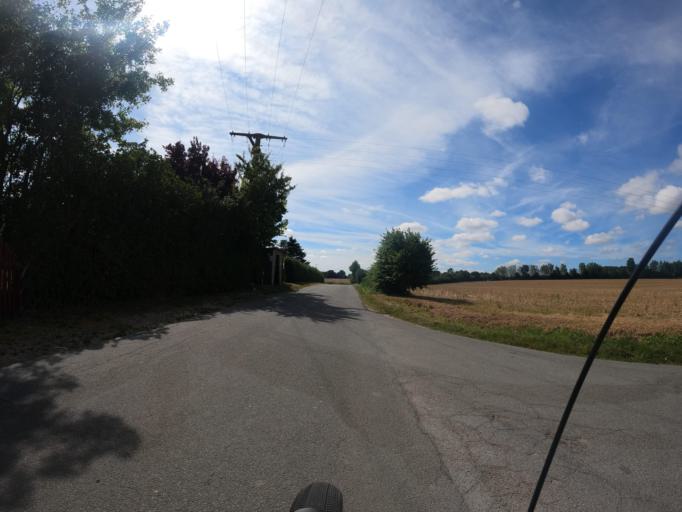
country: DE
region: Schleswig-Holstein
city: Steinbergkirche
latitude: 54.7893
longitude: 9.7456
